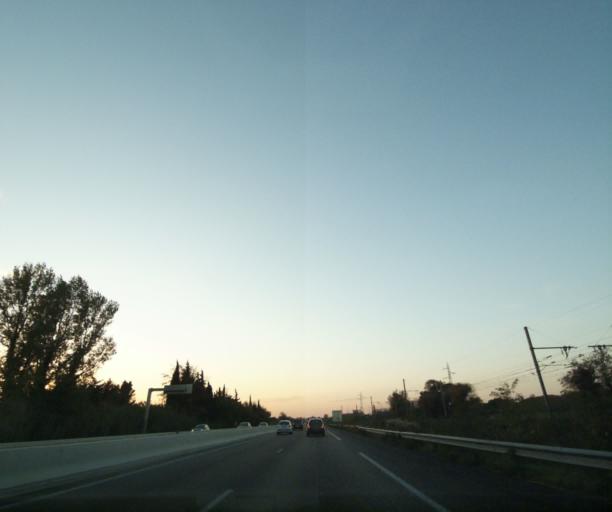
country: FR
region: Provence-Alpes-Cote d'Azur
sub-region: Departement des Bouches-du-Rhone
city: Arles
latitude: 43.6528
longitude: 4.6665
